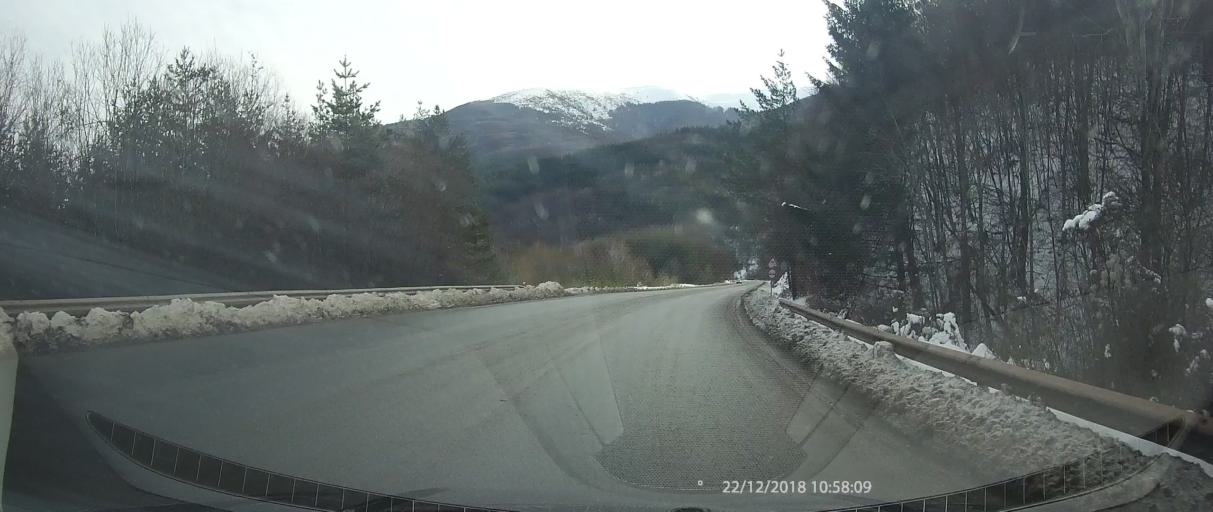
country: MK
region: Kriva Palanka
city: Kriva Palanka
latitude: 42.2188
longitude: 22.4661
